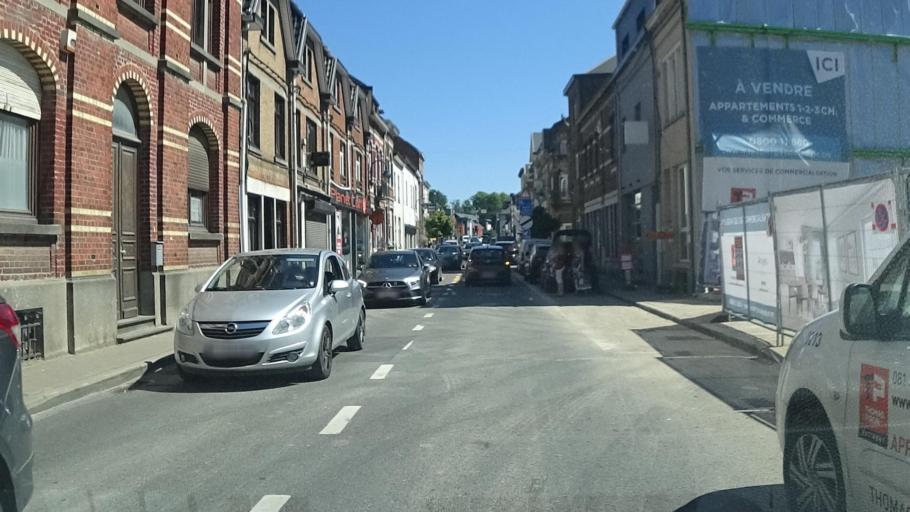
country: BE
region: Wallonia
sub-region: Province du Brabant Wallon
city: Court-Saint-Etienne
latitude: 50.6475
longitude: 4.5645
